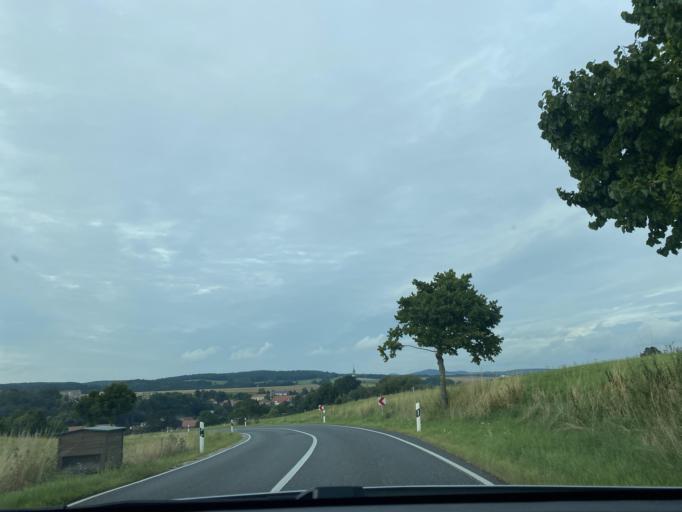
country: DE
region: Saxony
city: Bernstadt
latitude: 51.0414
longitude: 14.8197
